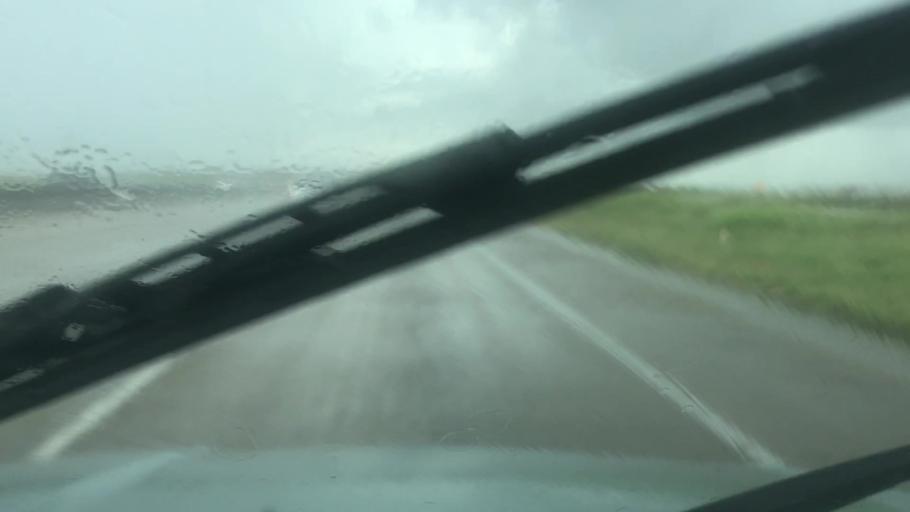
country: US
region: Texas
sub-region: Waller County
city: Brookshire
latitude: 29.7774
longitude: -95.8973
